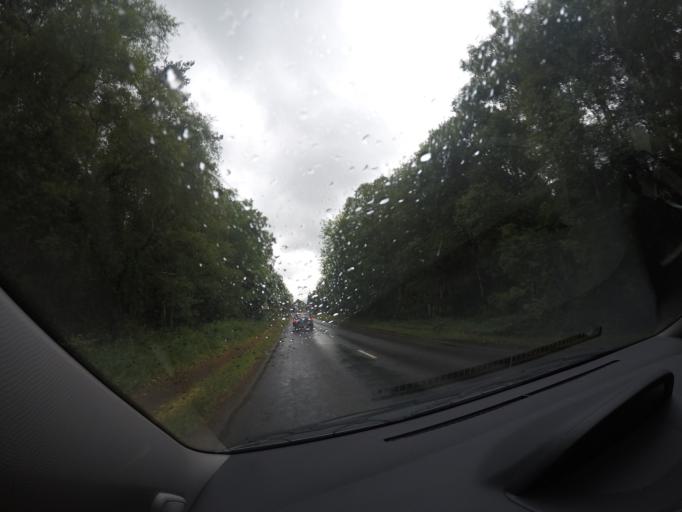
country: GB
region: Scotland
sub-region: Angus
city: Brechin
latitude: 56.8040
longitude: -2.6531
